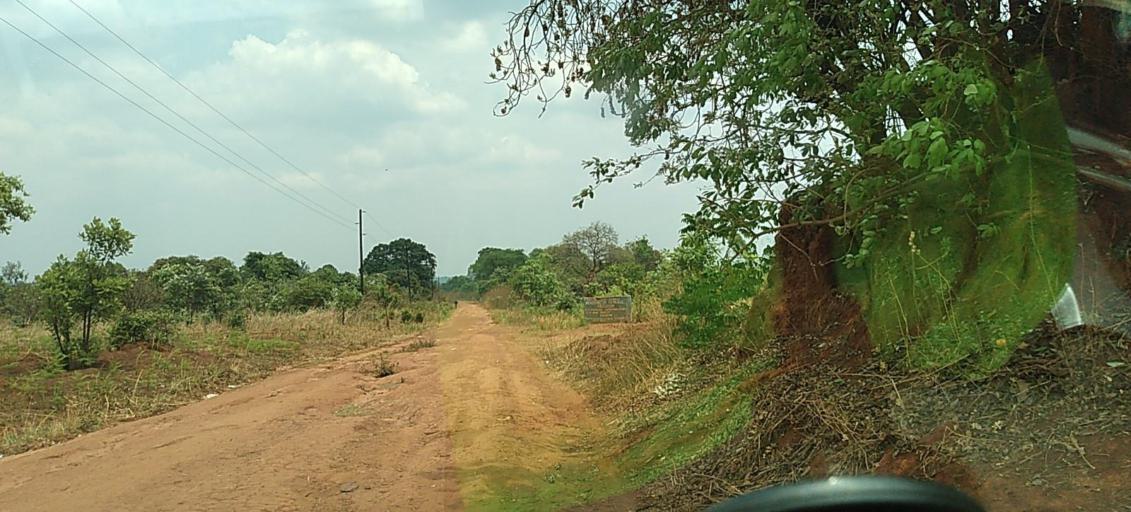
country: ZM
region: North-Western
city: Kansanshi
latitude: -12.0375
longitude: 26.4005
